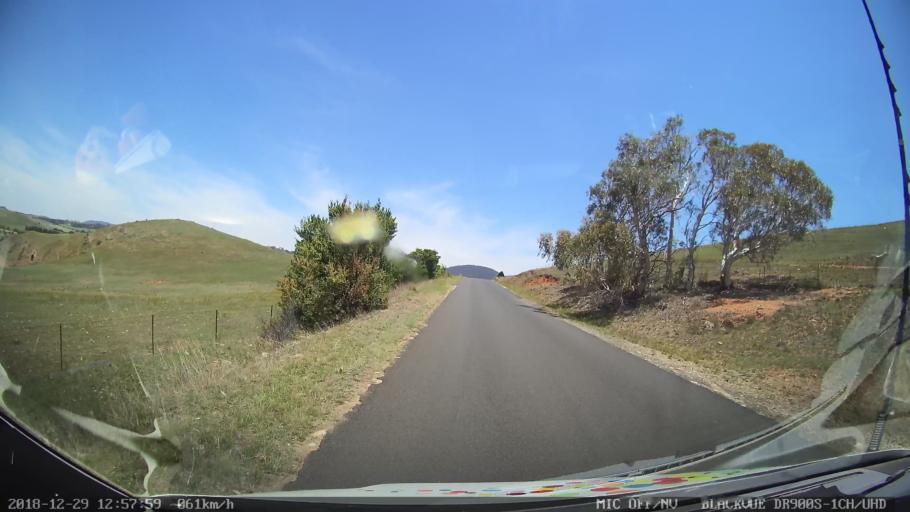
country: AU
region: Australian Capital Territory
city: Macarthur
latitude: -35.7097
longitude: 149.1717
